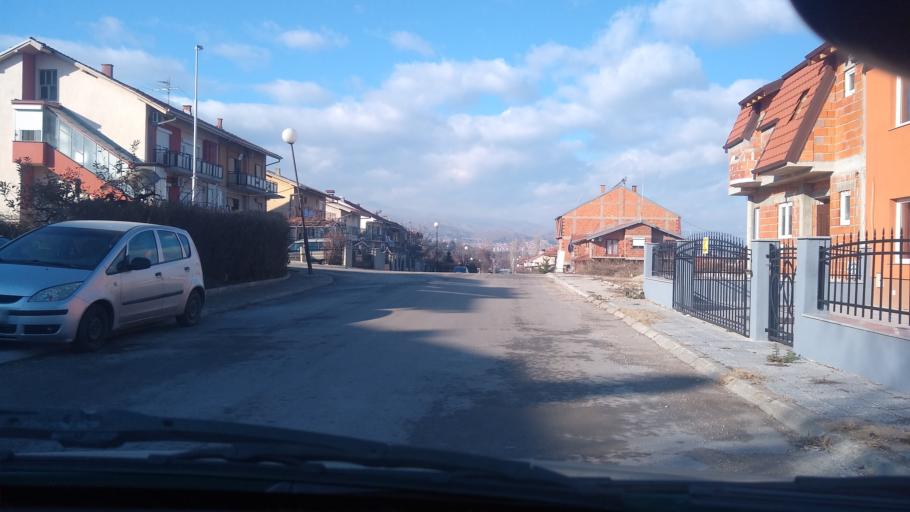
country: MK
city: Bistrica
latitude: 41.0054
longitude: 21.3492
